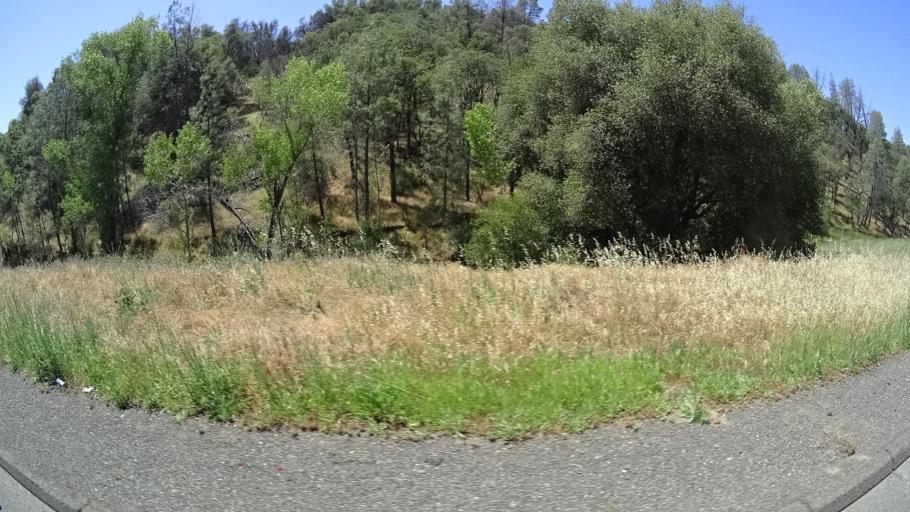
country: US
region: California
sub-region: Lake County
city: Hidden Valley Lake
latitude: 38.8260
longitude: -122.5812
